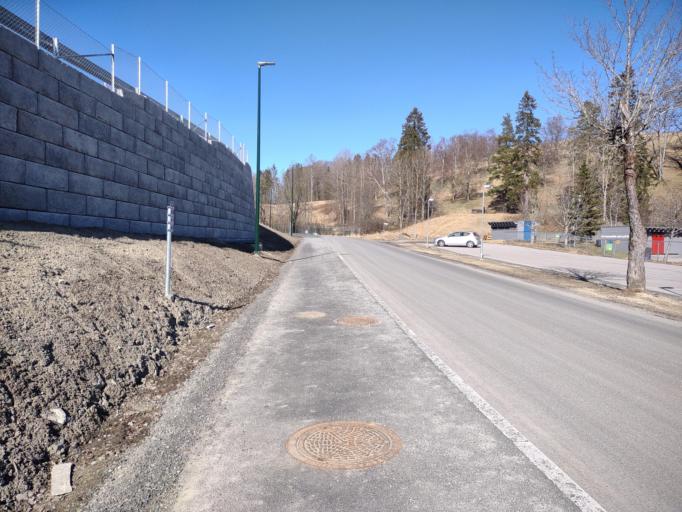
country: NO
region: Akershus
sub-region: Skedsmo
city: Lillestrom
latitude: 59.9767
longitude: 11.0333
